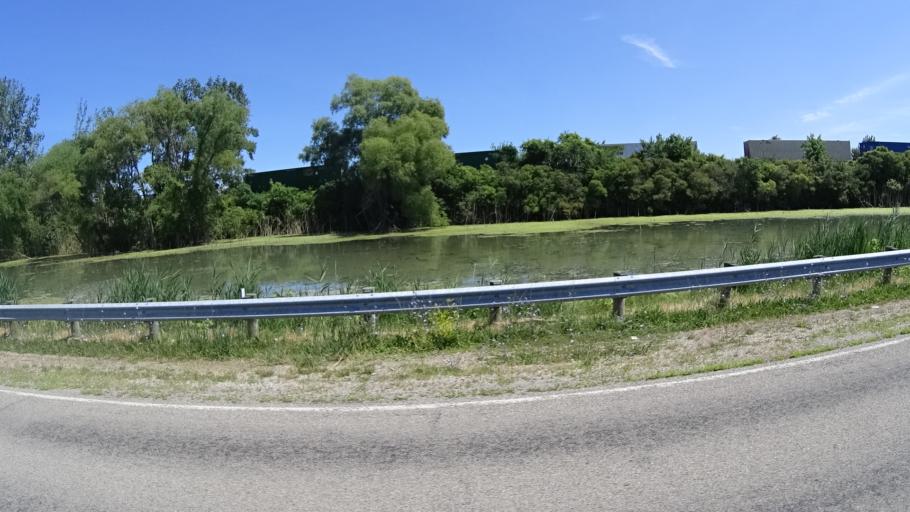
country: US
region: Ohio
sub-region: Erie County
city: Sandusky
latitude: 41.4668
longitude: -82.8052
